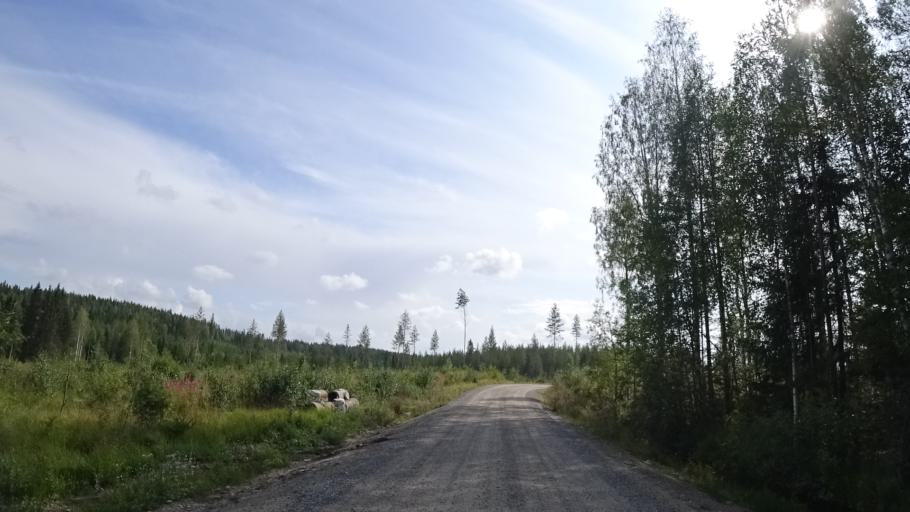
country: FI
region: North Karelia
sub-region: Pielisen Karjala
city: Lieksa
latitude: 63.5827
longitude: 30.1328
